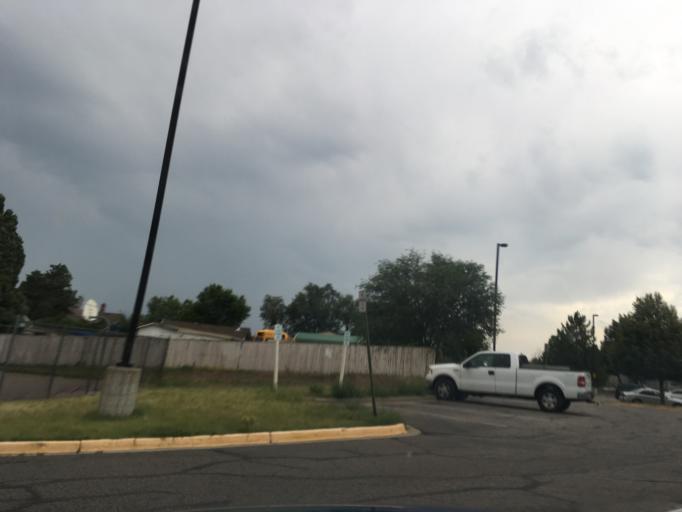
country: US
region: Colorado
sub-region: Arapahoe County
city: Sheridan
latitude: 39.6559
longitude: -105.0275
